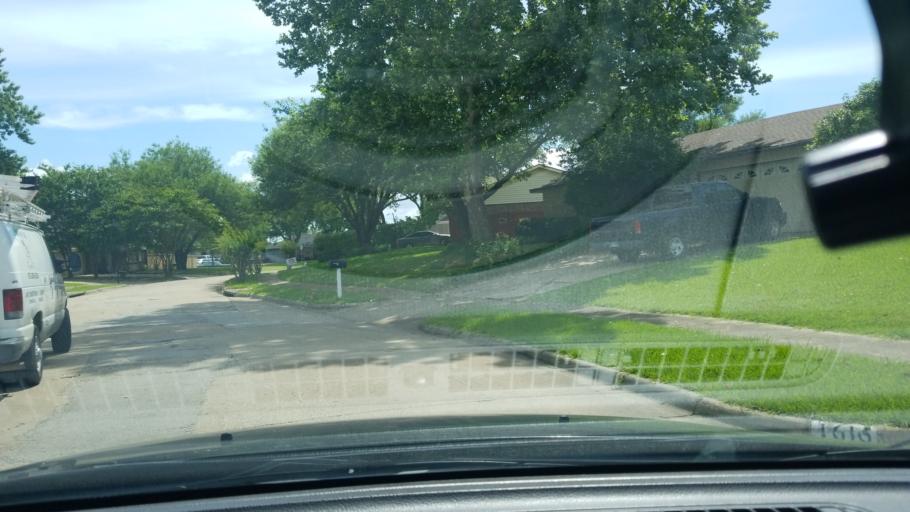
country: US
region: Texas
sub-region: Dallas County
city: Mesquite
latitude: 32.7566
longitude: -96.5767
